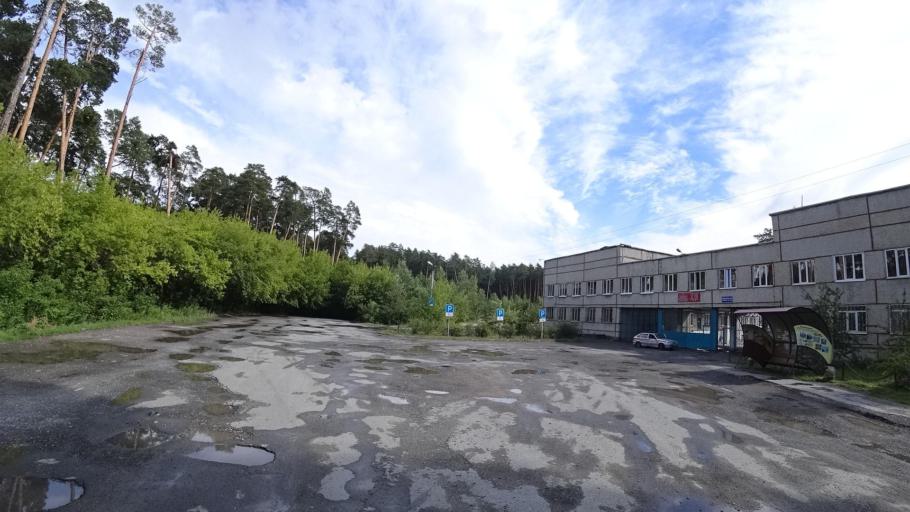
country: RU
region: Sverdlovsk
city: Kamyshlov
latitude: 56.8361
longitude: 62.7379
